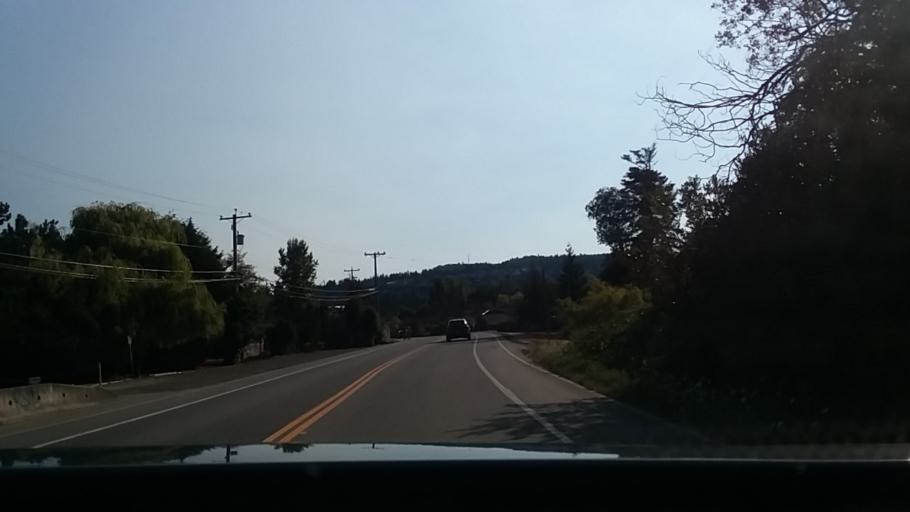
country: CA
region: British Columbia
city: North Saanich
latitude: 48.6340
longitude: -123.4075
